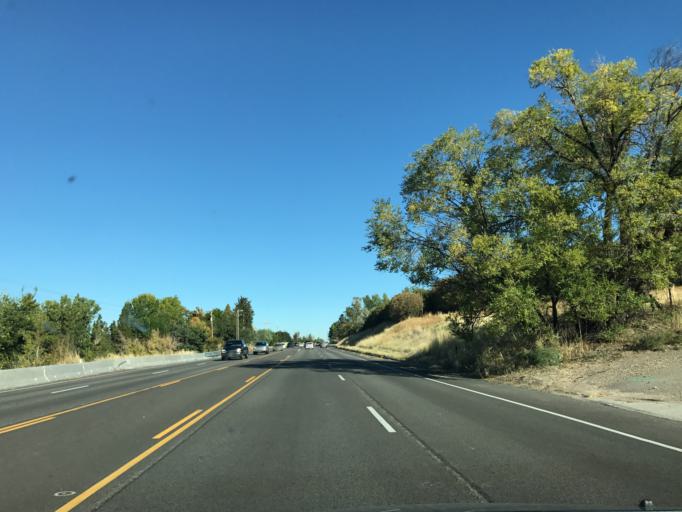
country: US
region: Utah
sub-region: Weber County
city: Washington Terrace
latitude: 41.1693
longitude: -111.9459
